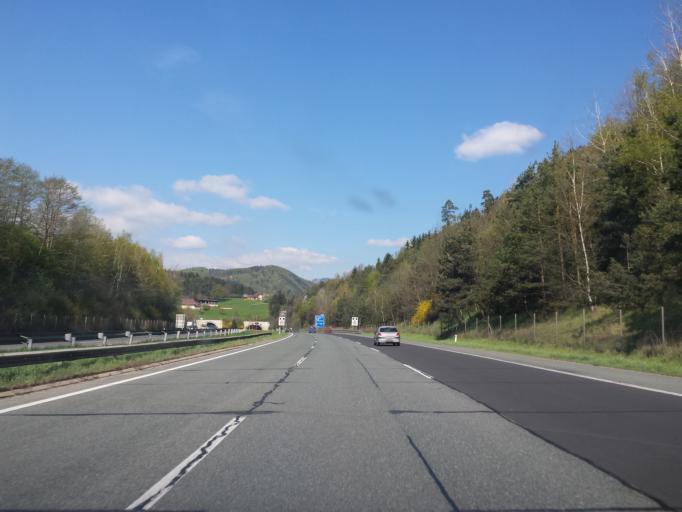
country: AT
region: Styria
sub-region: Politischer Bezirk Graz-Umgebung
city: Gratkorn
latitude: 47.1392
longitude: 15.3510
